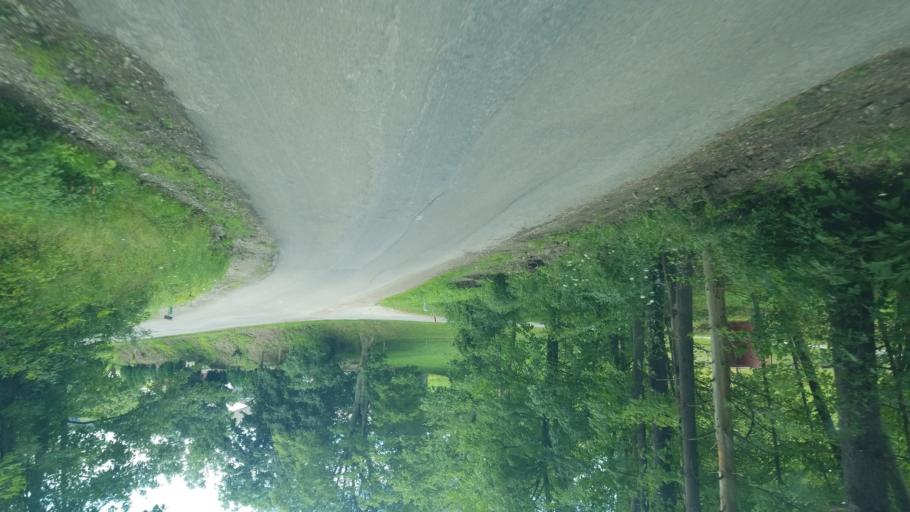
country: US
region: Ohio
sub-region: Holmes County
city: Millersburg
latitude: 40.5134
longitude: -81.8029
